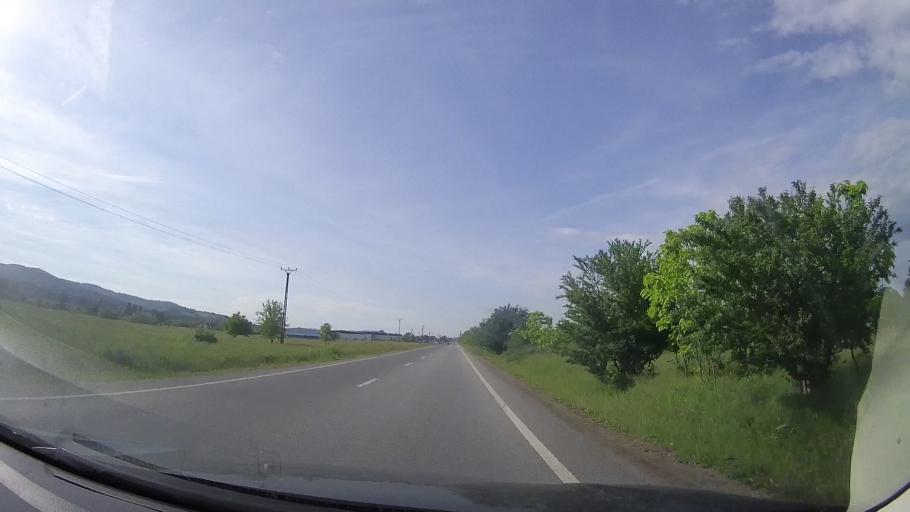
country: RO
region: Caras-Severin
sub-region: Comuna Buchin
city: Buchin
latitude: 45.3764
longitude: 22.2352
